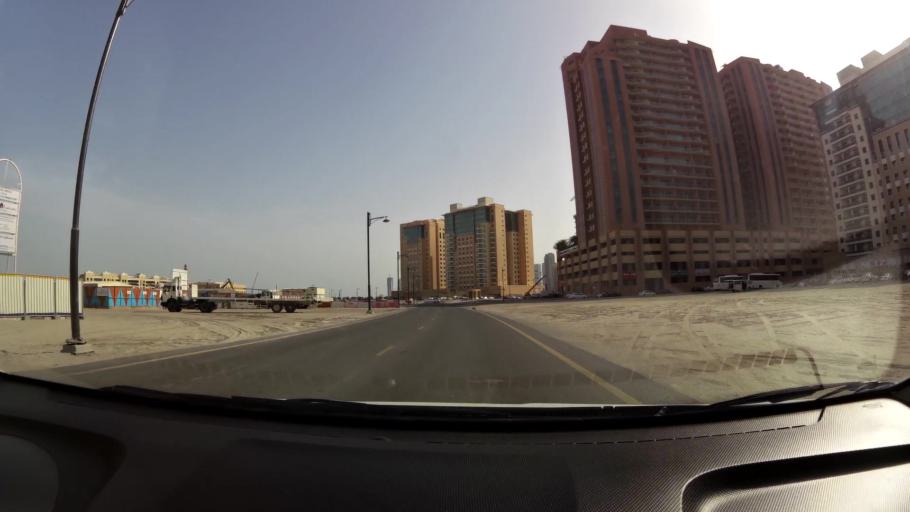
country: AE
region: Ash Shariqah
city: Sharjah
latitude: 25.2858
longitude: 55.3565
